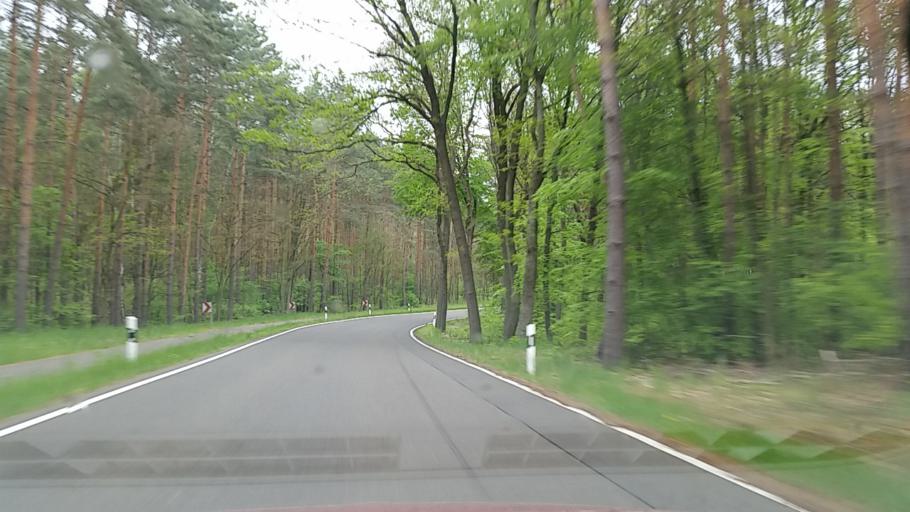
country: DE
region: Brandenburg
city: Reichenwalde
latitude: 52.3097
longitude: 13.9668
